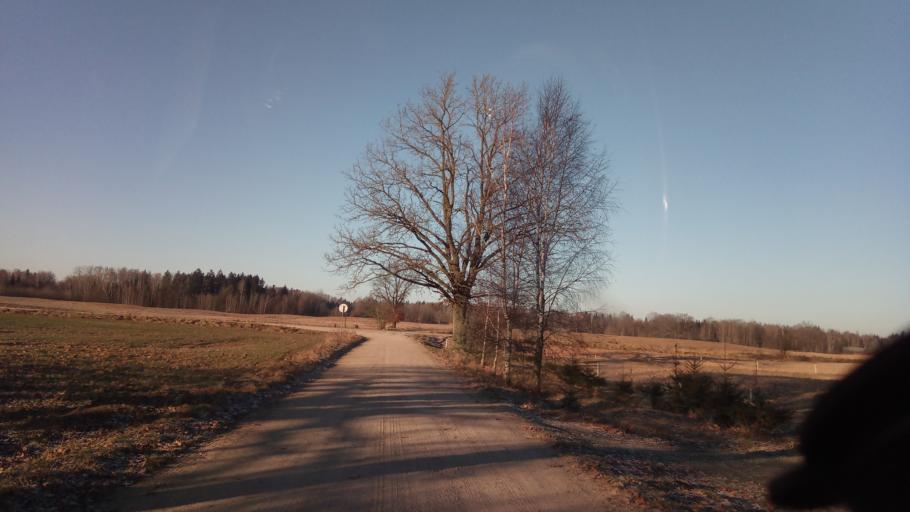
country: LT
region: Alytaus apskritis
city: Druskininkai
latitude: 54.1011
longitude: 24.0083
